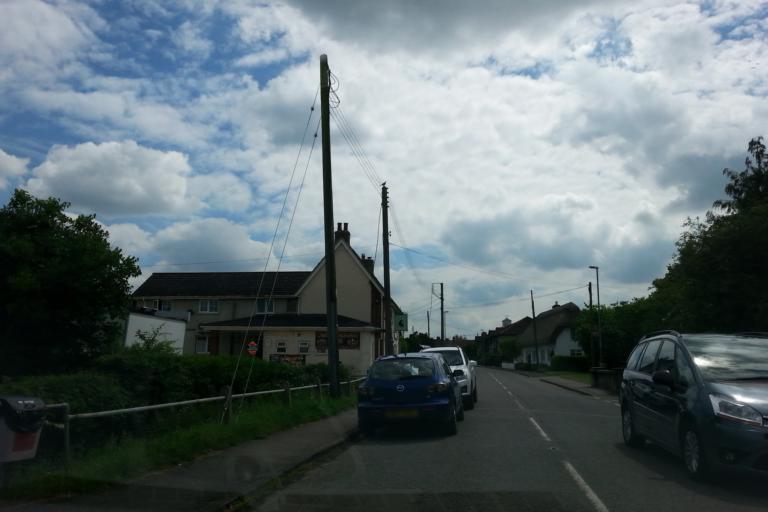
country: GB
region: England
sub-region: Cambridgeshire
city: Swavesey
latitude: 52.2827
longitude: 0.0444
